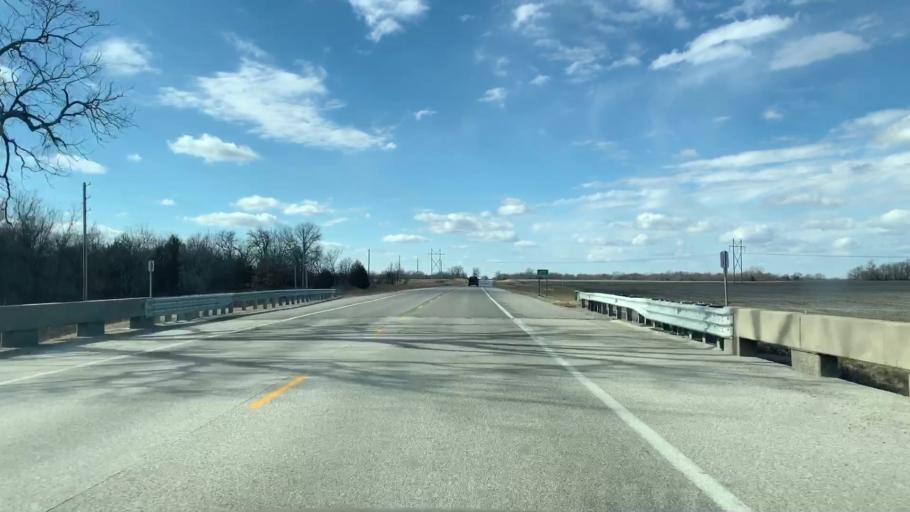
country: US
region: Kansas
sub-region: Labette County
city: Oswego
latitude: 37.3400
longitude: -95.0745
